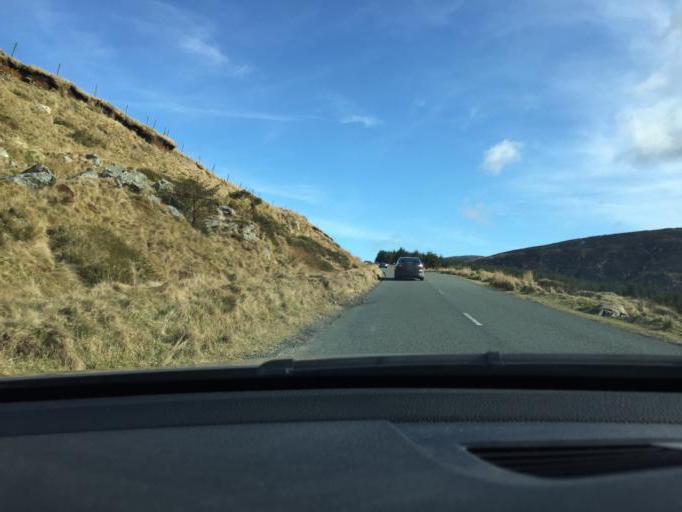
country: IE
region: Leinster
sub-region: Wicklow
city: Valleymount
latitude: 53.0484
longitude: -6.4072
